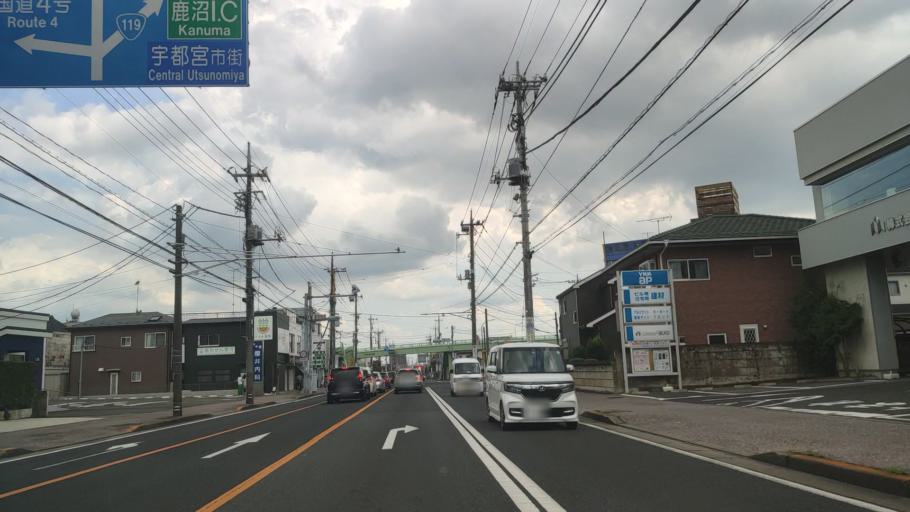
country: JP
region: Tochigi
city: Utsunomiya-shi
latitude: 36.5759
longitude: 139.8711
